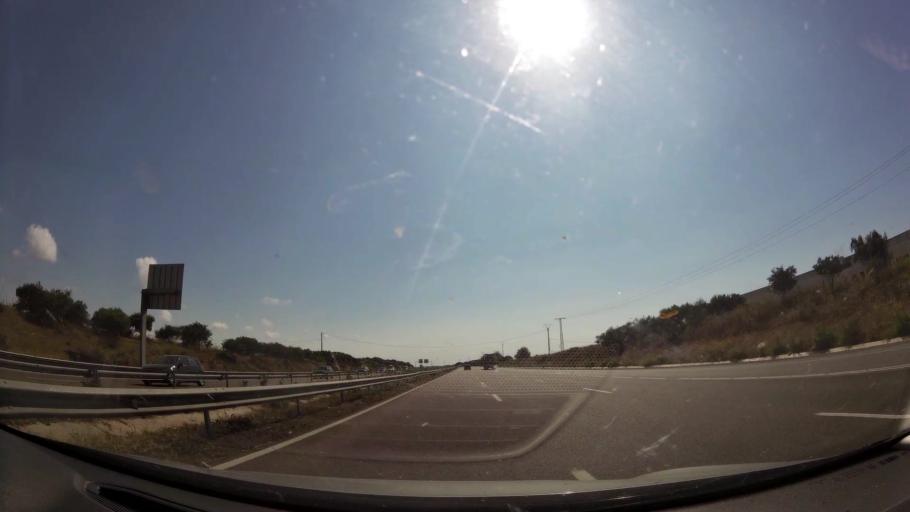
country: MA
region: Chaouia-Ouardigha
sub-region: Benslimane
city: Bouznika
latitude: 33.8193
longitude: -7.1219
